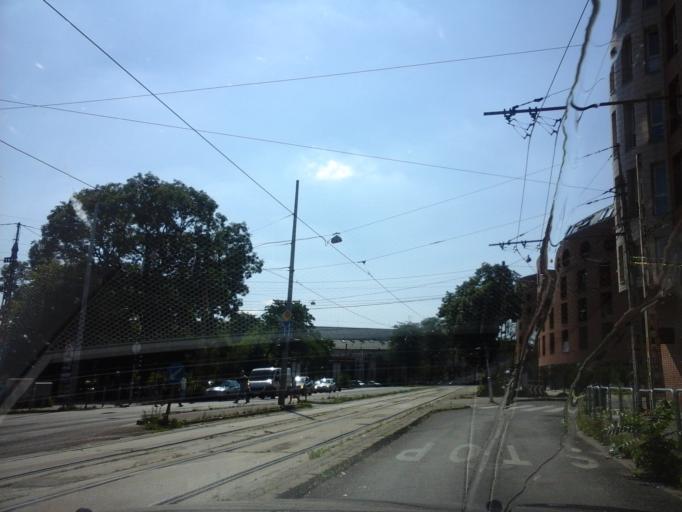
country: HU
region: Budapest
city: Budapest VIII. keruelet
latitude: 47.4893
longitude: 19.0911
